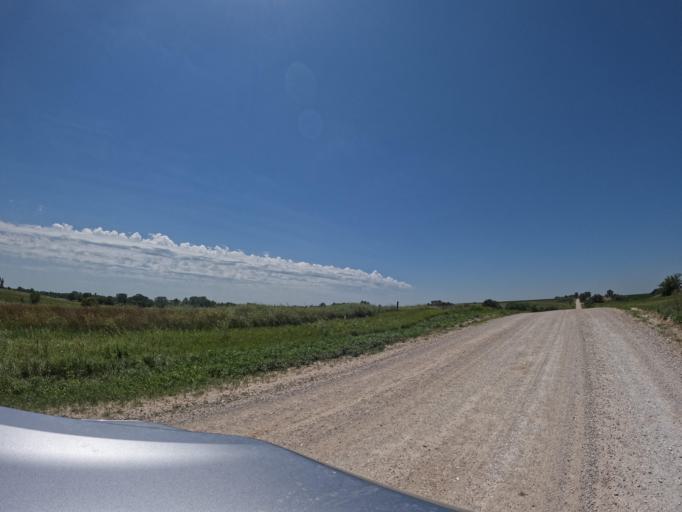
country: US
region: Iowa
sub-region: Keokuk County
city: Sigourney
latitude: 41.4089
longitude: -92.3288
